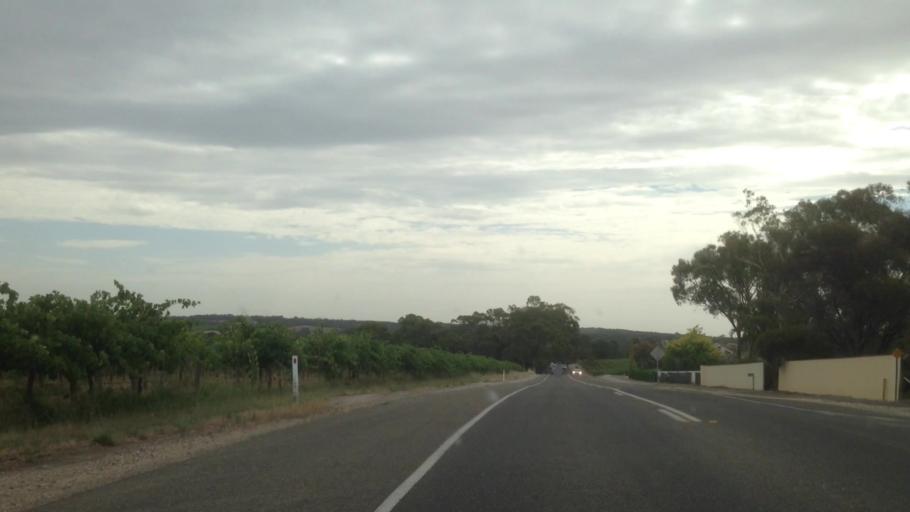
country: AU
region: South Australia
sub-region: Barossa
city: Lyndoch
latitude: -34.5971
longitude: 138.9137
